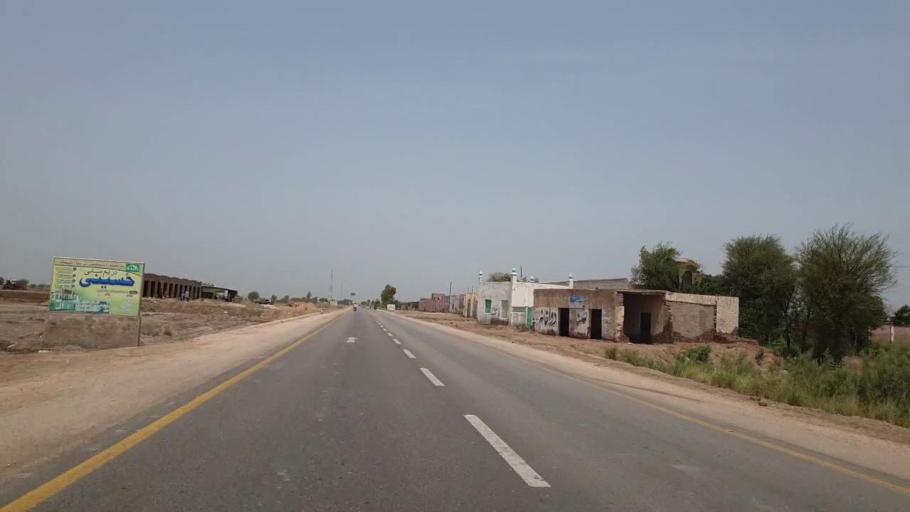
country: PK
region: Sindh
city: Shahpur Chakar
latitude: 26.1951
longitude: 68.5679
